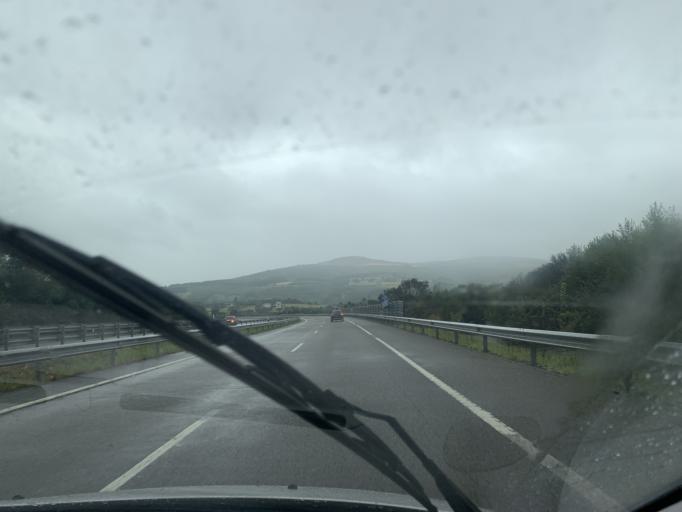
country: ES
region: Galicia
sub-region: Provincia de Lugo
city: Abadin
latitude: 43.3597
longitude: -7.4706
